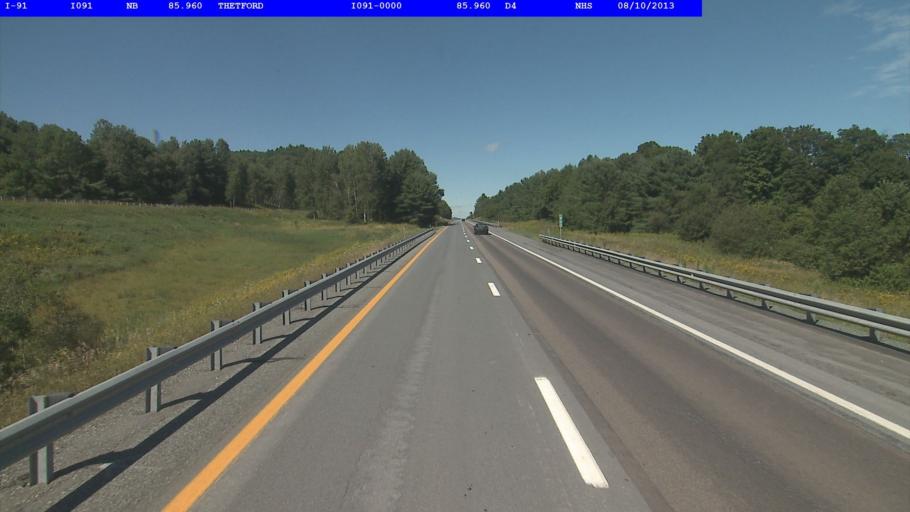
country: US
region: New Hampshire
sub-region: Grafton County
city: Lyme
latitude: 43.8362
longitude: -72.2041
